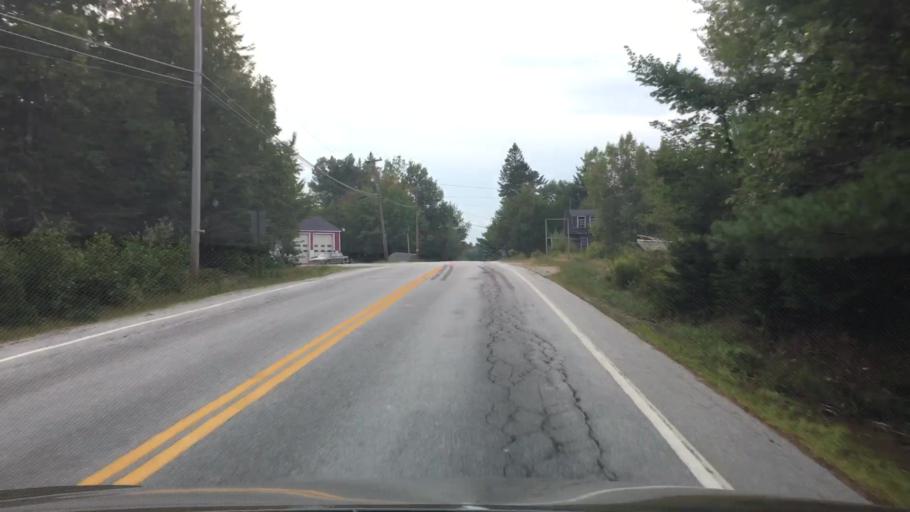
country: US
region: Maine
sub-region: Hancock County
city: Penobscot
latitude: 44.4473
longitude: -68.6153
